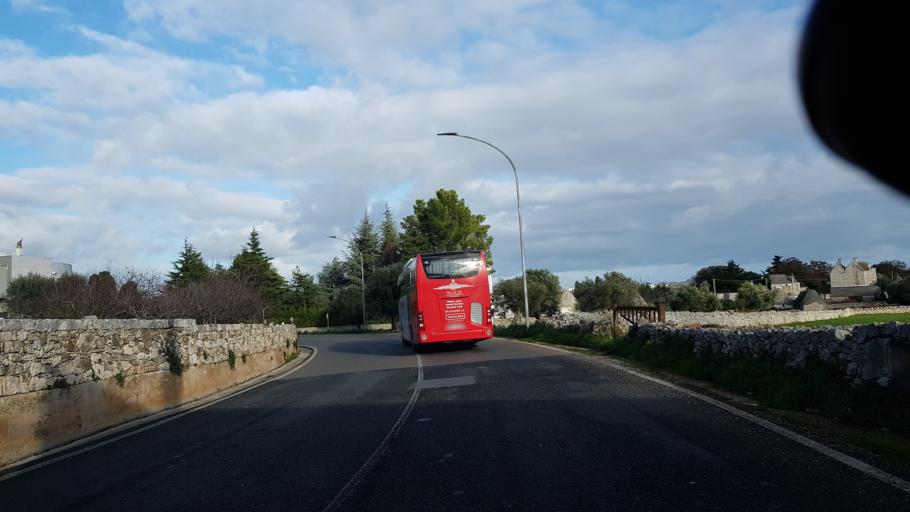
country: IT
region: Apulia
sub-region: Provincia di Bari
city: Alberobello
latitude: 40.7839
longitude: 17.2440
